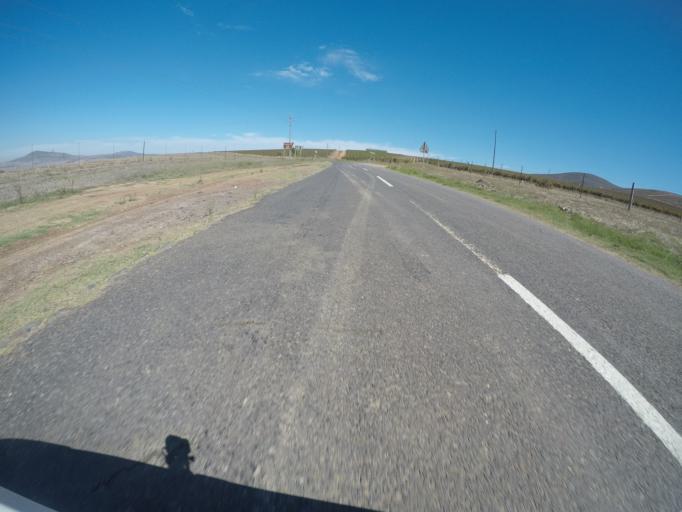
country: ZA
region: Western Cape
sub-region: City of Cape Town
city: Sunset Beach
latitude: -33.7099
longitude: 18.5831
